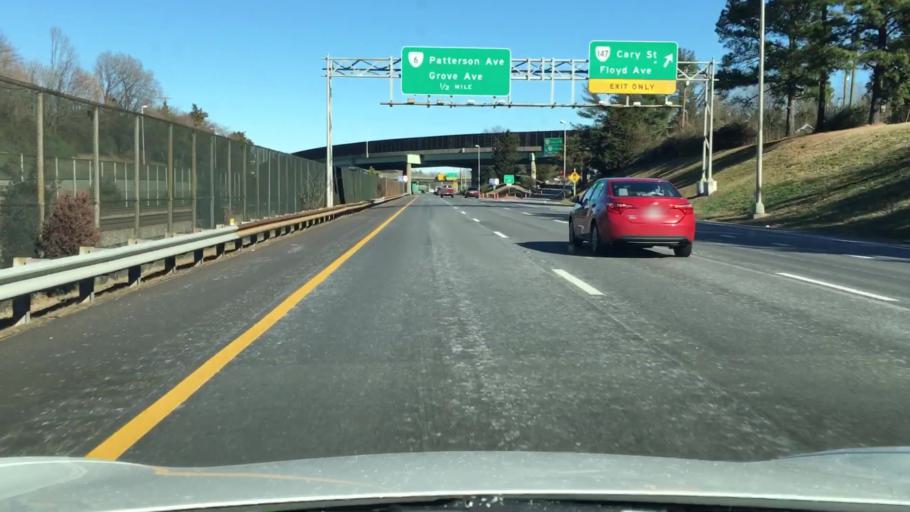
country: US
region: Virginia
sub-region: City of Richmond
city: Richmond
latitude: 37.5524
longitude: -77.4906
